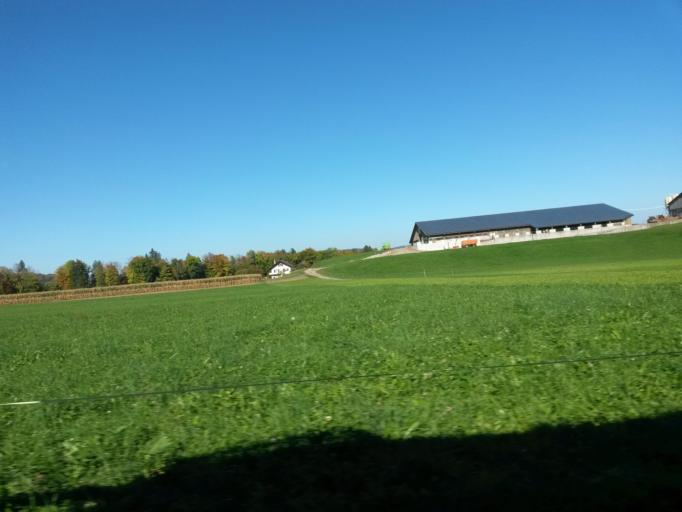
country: CH
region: Fribourg
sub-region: Gruyere District
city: Gruyeres
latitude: 46.5852
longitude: 7.0777
